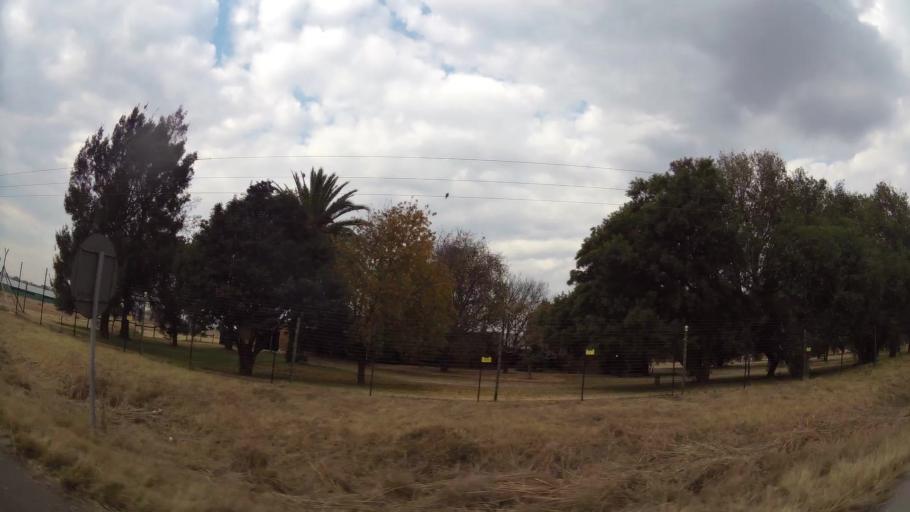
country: ZA
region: Mpumalanga
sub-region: Nkangala District Municipality
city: Delmas
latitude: -26.2974
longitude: 28.6071
